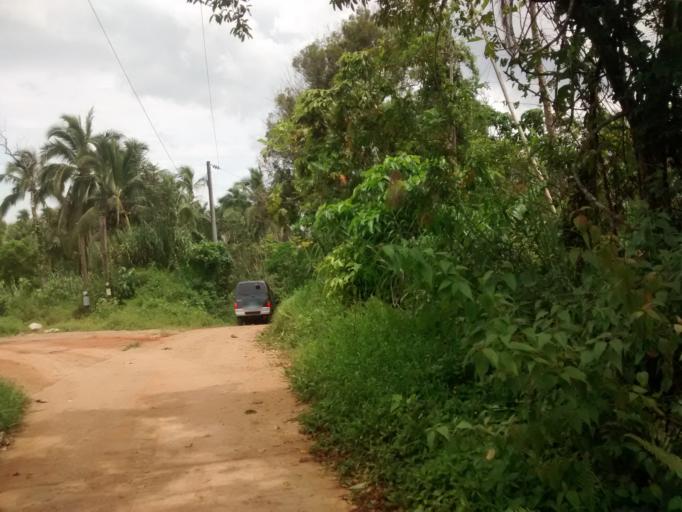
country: PH
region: Calabarzon
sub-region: Province of Quezon
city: Lucban
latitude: 14.1533
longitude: 121.5581
